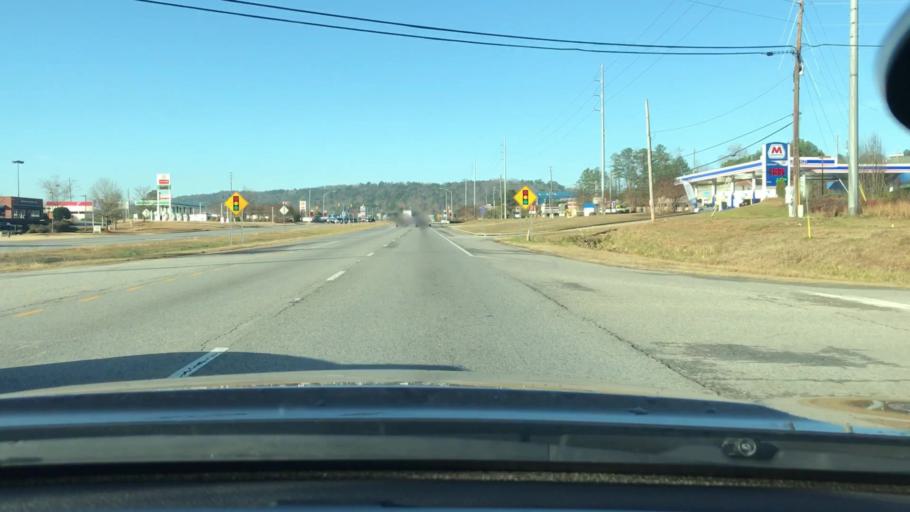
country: US
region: Alabama
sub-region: Shelby County
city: Chelsea
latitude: 33.3488
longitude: -86.6287
